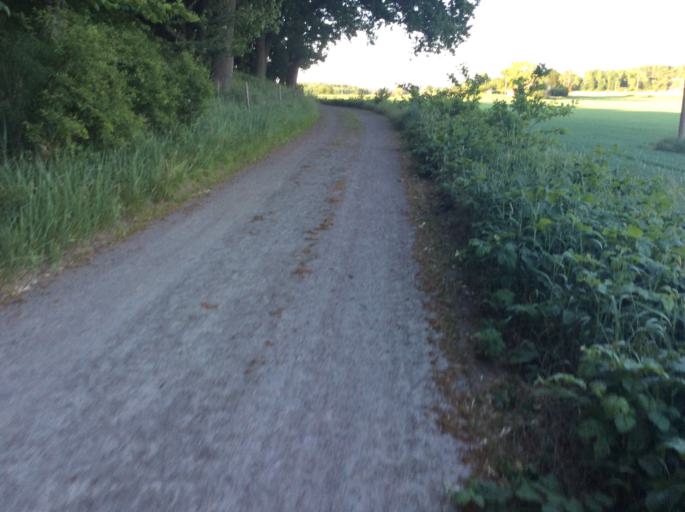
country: SE
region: Vaestra Goetaland
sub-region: Goteborg
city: Majorna
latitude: 57.7923
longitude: 11.8690
